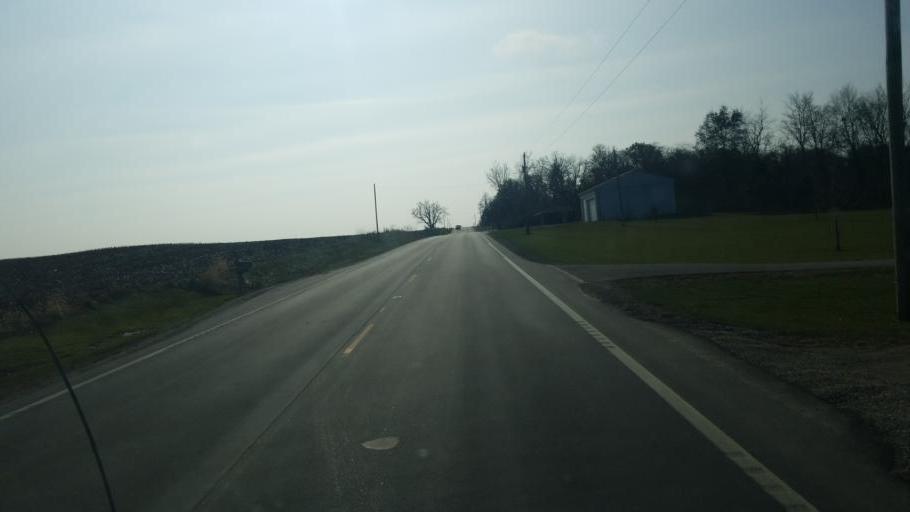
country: US
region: Ohio
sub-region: Mercer County
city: Fort Recovery
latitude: 40.4361
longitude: -84.7846
